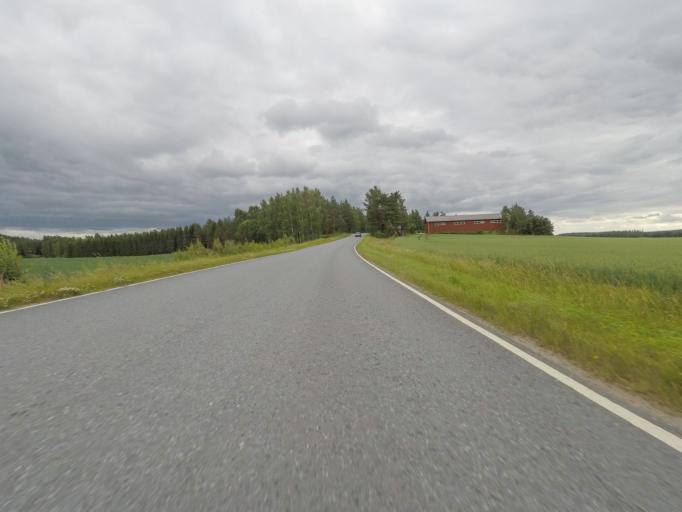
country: FI
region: Varsinais-Suomi
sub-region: Salo
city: Muurla
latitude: 60.3275
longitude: 23.2828
